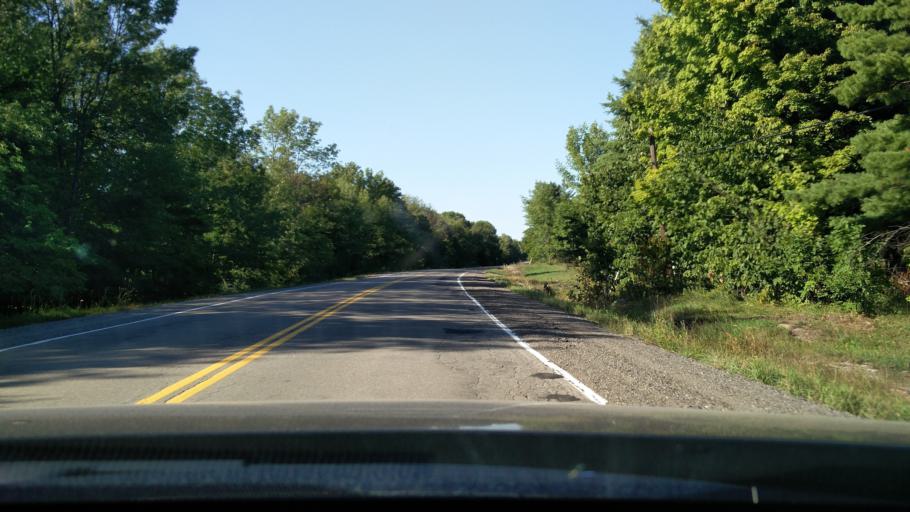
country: CA
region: Ontario
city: Perth
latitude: 44.7082
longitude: -76.4008
